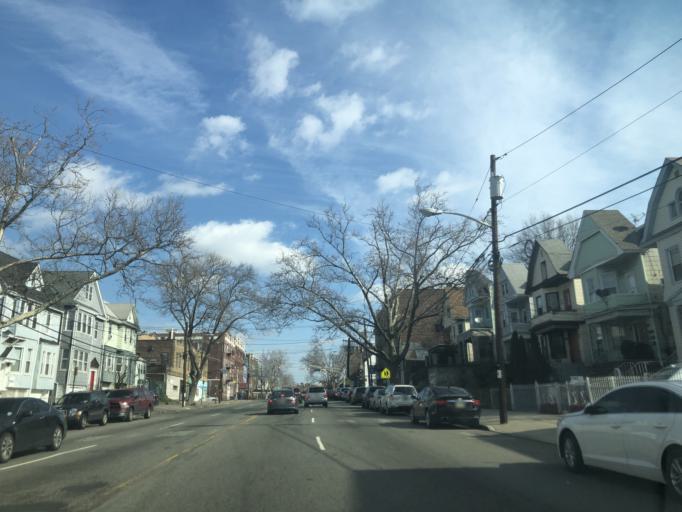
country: US
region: New Jersey
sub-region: Hudson County
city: Jersey City
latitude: 40.7151
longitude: -74.0824
